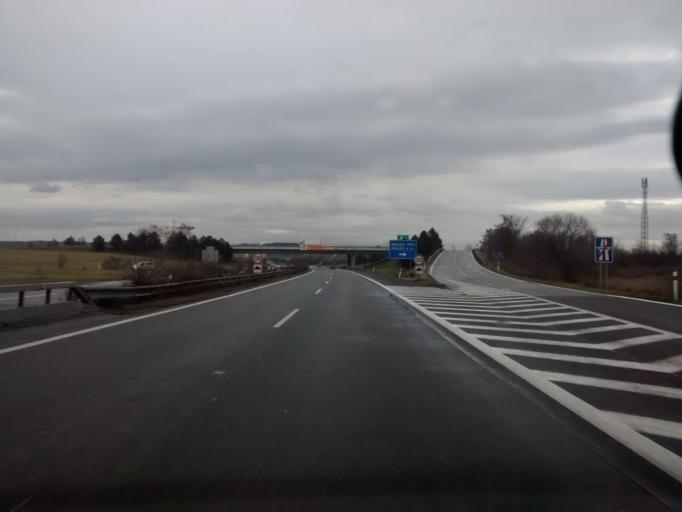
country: CZ
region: Central Bohemia
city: Odolena Voda
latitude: 50.2487
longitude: 14.3735
